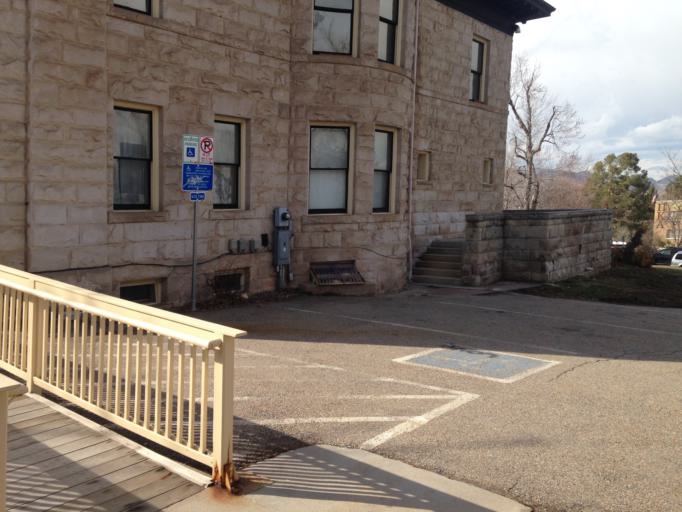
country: US
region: Colorado
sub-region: Boulder County
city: Boulder
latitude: 40.0050
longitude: -105.2770
